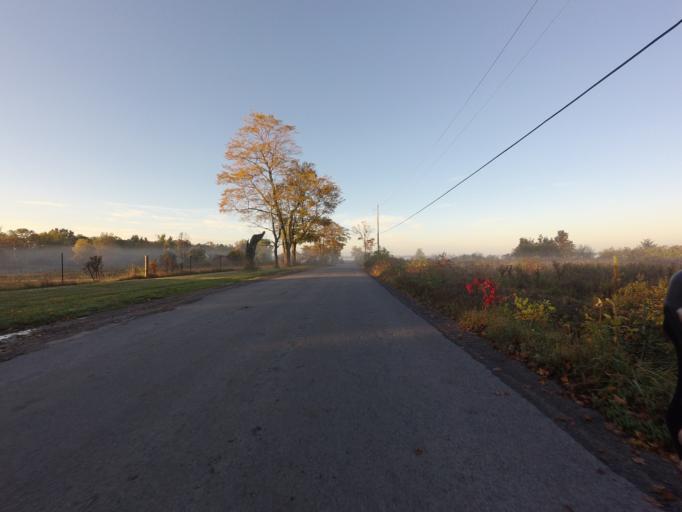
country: CA
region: Ontario
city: Quinte West
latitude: 44.0375
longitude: -77.5930
